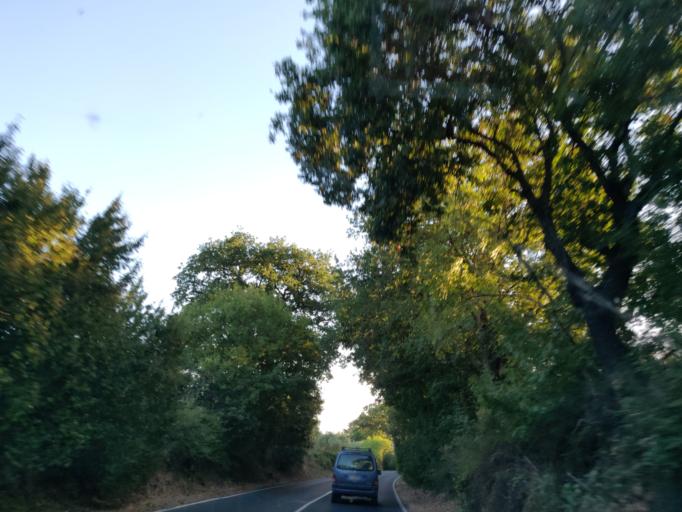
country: IT
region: Latium
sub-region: Provincia di Viterbo
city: Canino
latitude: 42.4407
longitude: 11.7303
